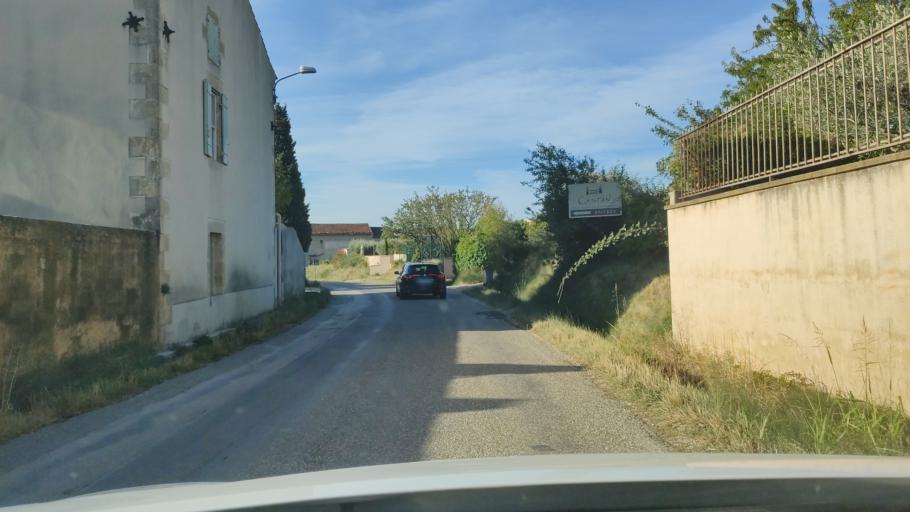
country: FR
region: Languedoc-Roussillon
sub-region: Departement du Gard
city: Saze
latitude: 43.9331
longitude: 4.6513
